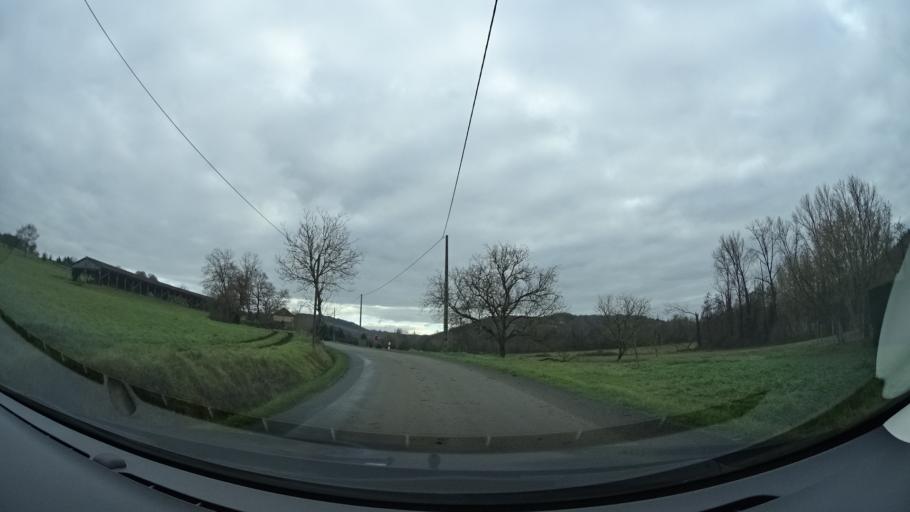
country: FR
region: Aquitaine
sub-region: Departement de la Dordogne
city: Belves
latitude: 44.8155
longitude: 0.9992
